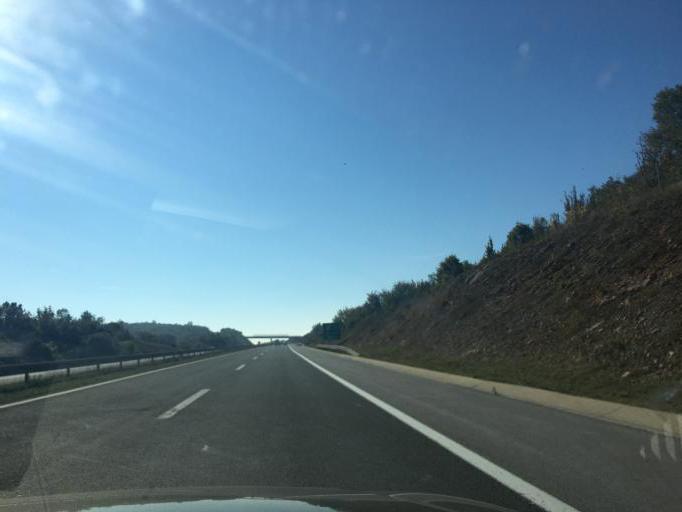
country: HR
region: Licko-Senjska
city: Gospic
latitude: 44.6874
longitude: 15.4056
